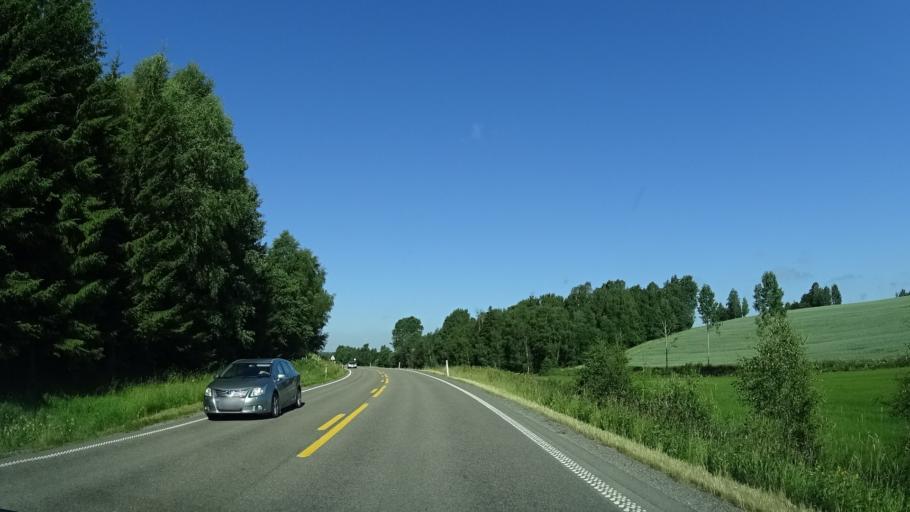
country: NO
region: Akershus
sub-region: Ski
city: Ski
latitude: 59.6834
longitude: 10.8472
